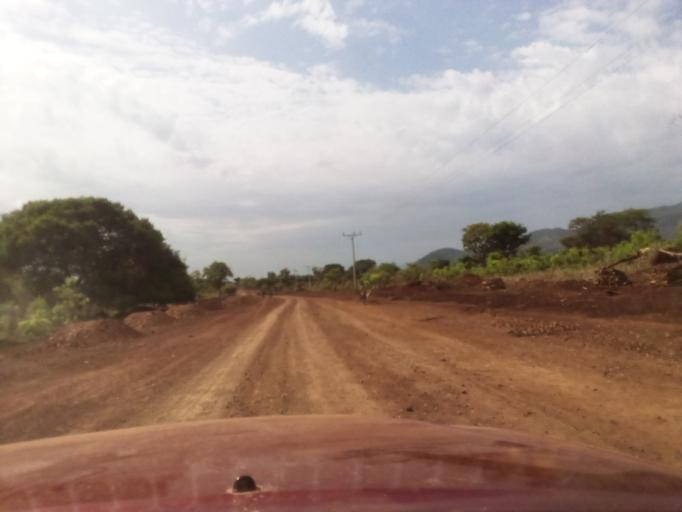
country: ET
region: Oromiya
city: Mendi
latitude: 10.0567
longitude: 35.2864
